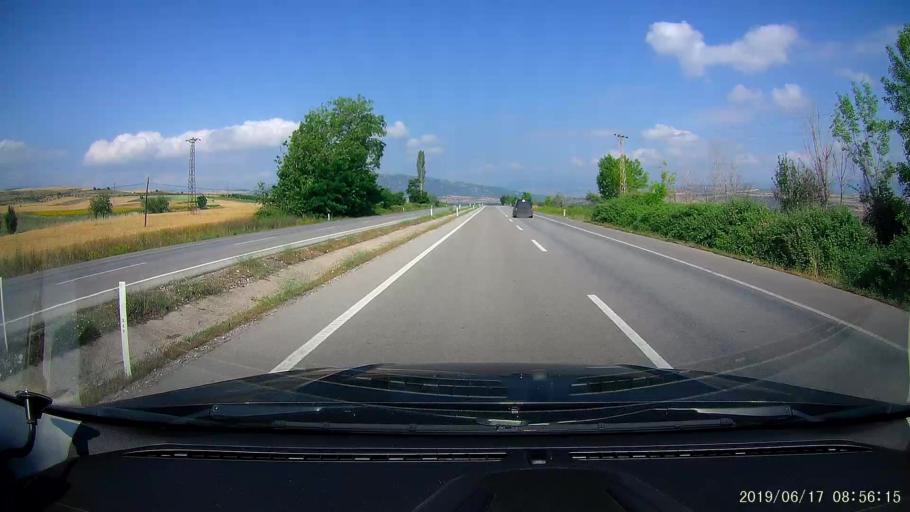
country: TR
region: Amasya
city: Esencay
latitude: 40.7336
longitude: 36.4261
